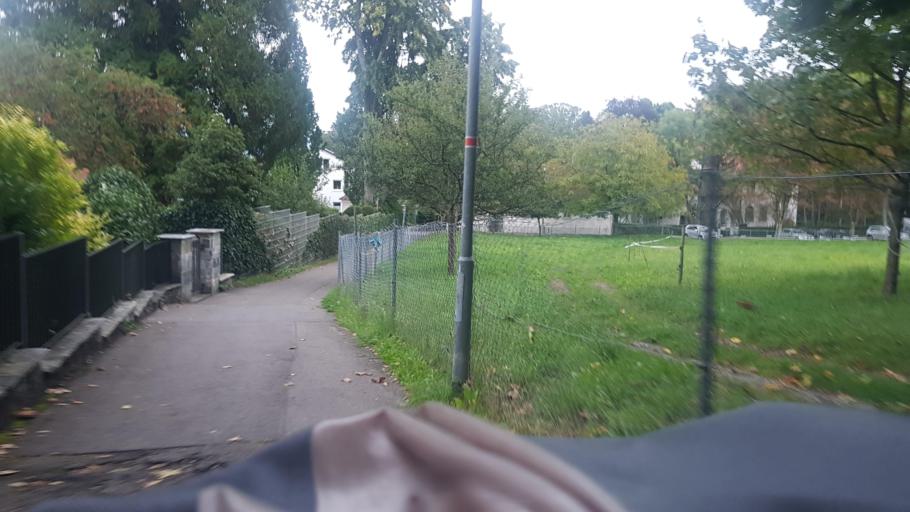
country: DE
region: Bavaria
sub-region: Swabia
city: Bodolz
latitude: 47.5596
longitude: 9.6747
